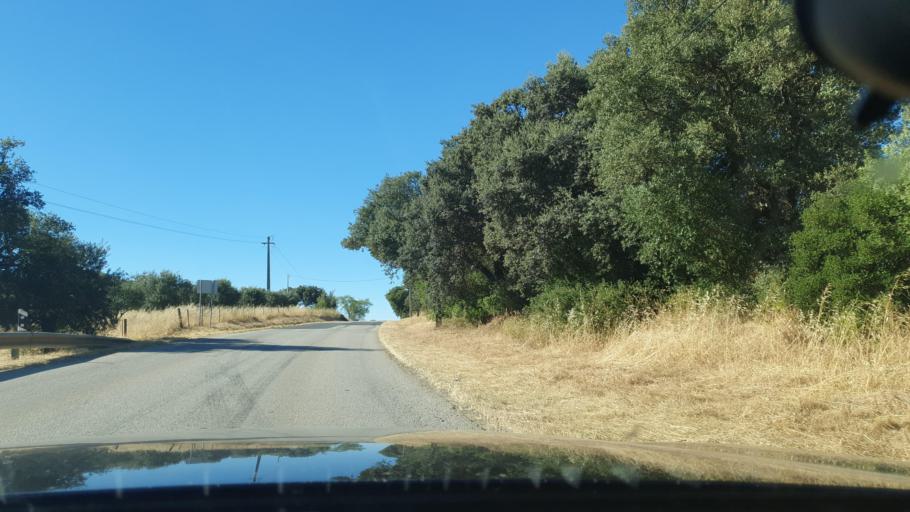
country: PT
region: Evora
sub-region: Alandroal
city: Alandroal
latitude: 38.7109
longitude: -7.4063
